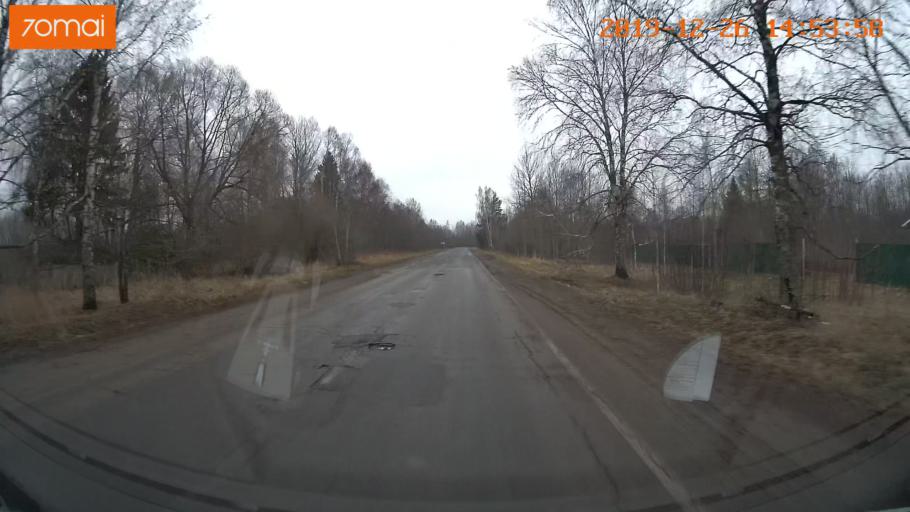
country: RU
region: Jaroslavl
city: Rybinsk
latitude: 58.3110
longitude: 38.8865
